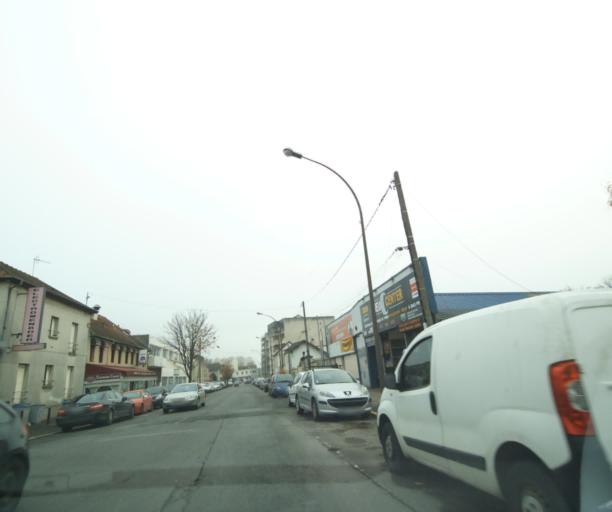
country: FR
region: Ile-de-France
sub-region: Departement de Seine-Saint-Denis
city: Livry-Gargan
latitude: 48.9275
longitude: 2.5479
